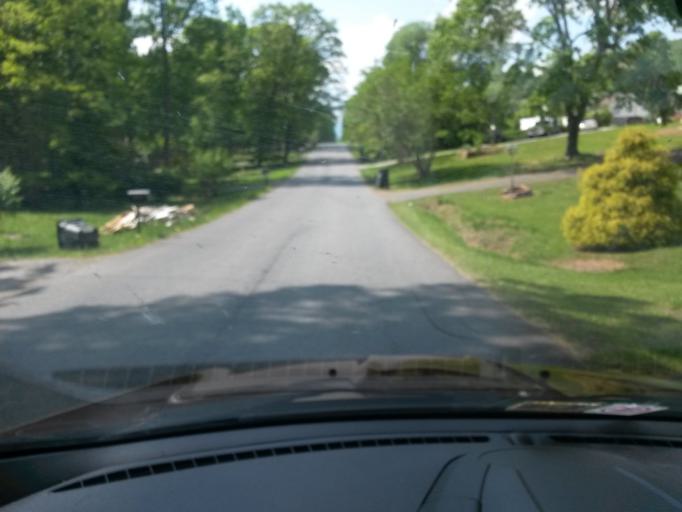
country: US
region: Virginia
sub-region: Campbell County
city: Timberlake
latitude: 37.3371
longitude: -79.2145
